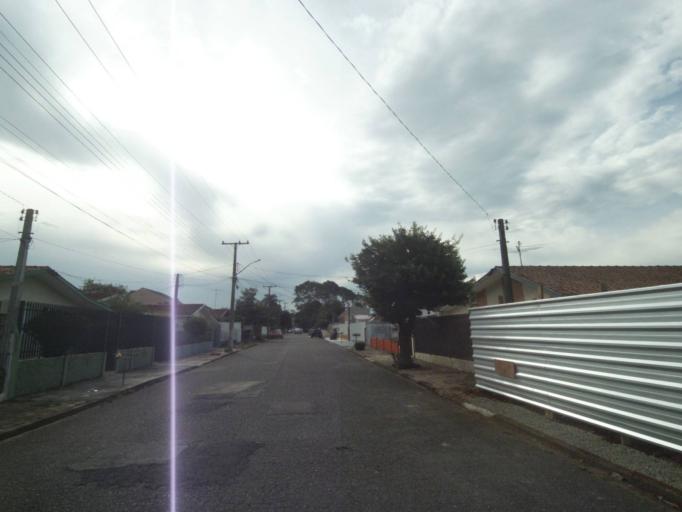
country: BR
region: Parana
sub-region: Curitiba
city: Curitiba
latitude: -25.4299
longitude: -49.2324
